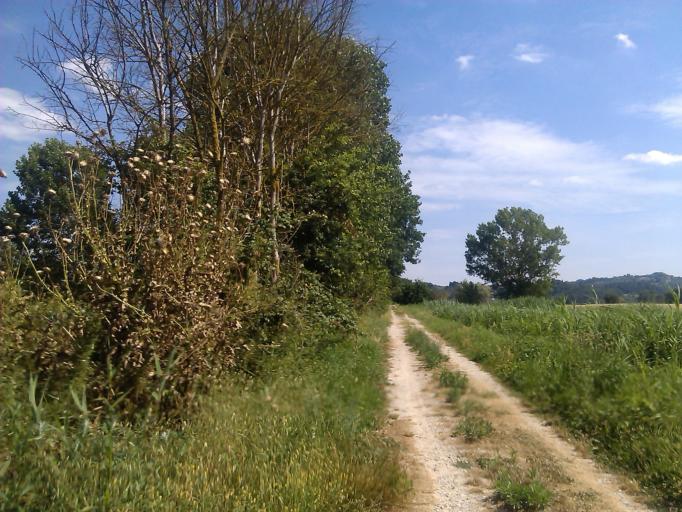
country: IT
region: Tuscany
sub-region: Provincia di Siena
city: Chiusi
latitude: 43.0582
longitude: 11.9350
